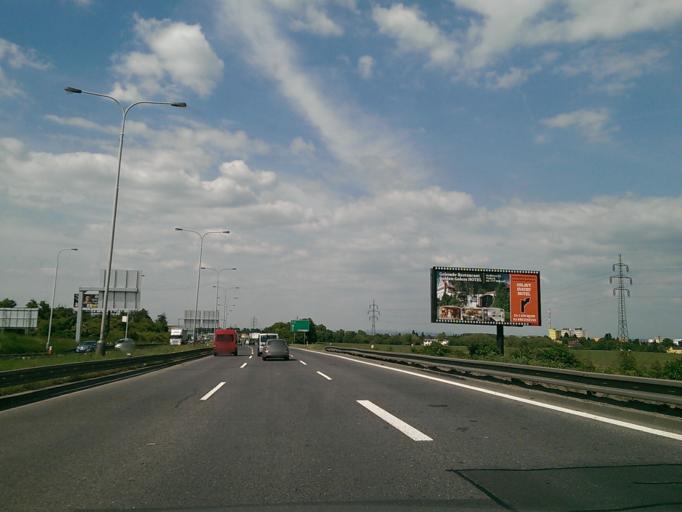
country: CZ
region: Praha
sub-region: Praha 9
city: Strizkov
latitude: 50.1408
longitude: 14.4946
